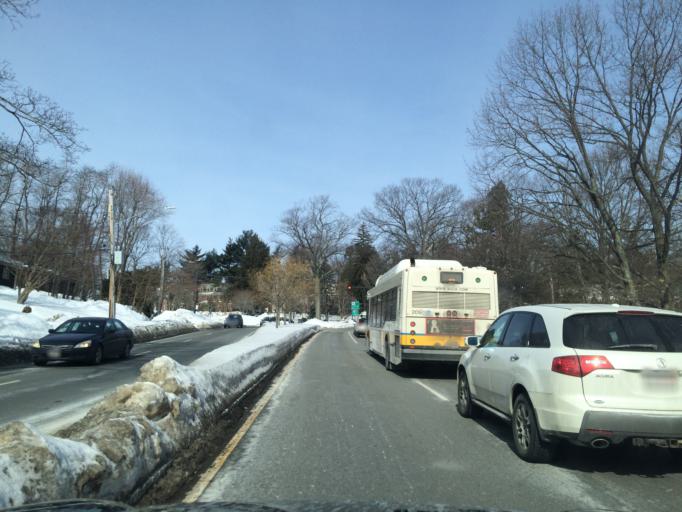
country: US
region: Massachusetts
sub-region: Norfolk County
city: Brookline
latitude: 42.3256
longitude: -71.1400
